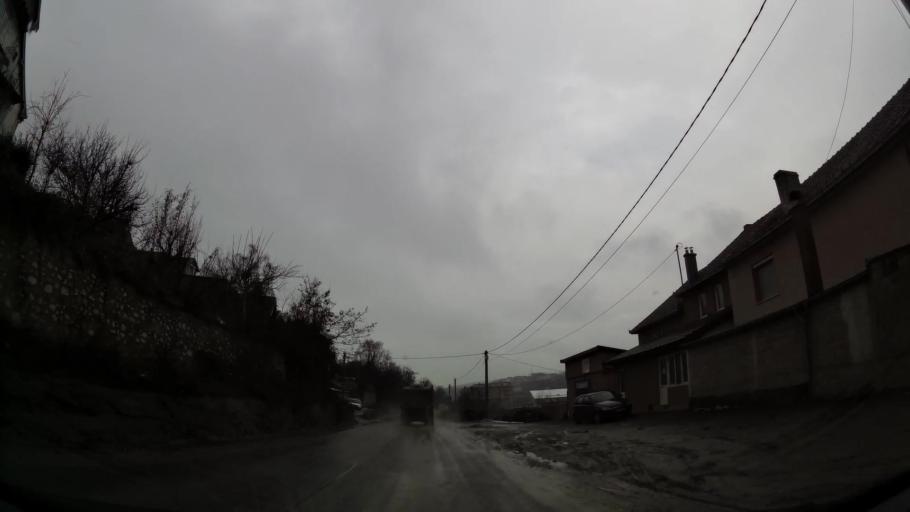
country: XK
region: Ferizaj
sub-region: Komuna e Kacanikut
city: Kacanik
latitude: 42.2258
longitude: 21.2545
